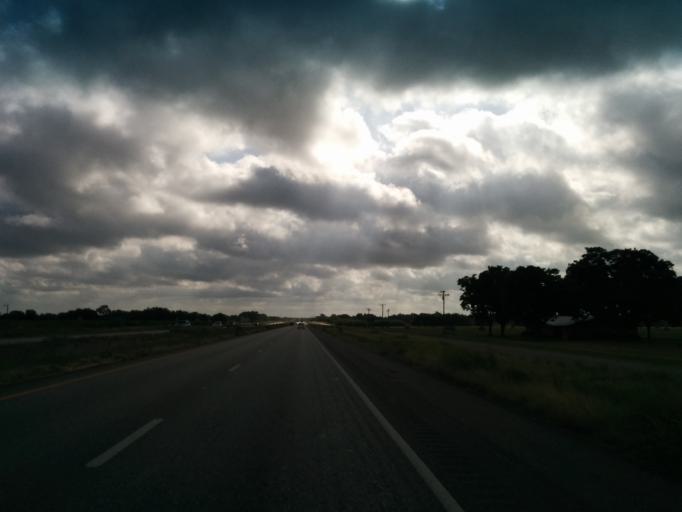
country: US
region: Texas
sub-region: Guadalupe County
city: Cibolo
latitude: 29.5027
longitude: -98.1818
